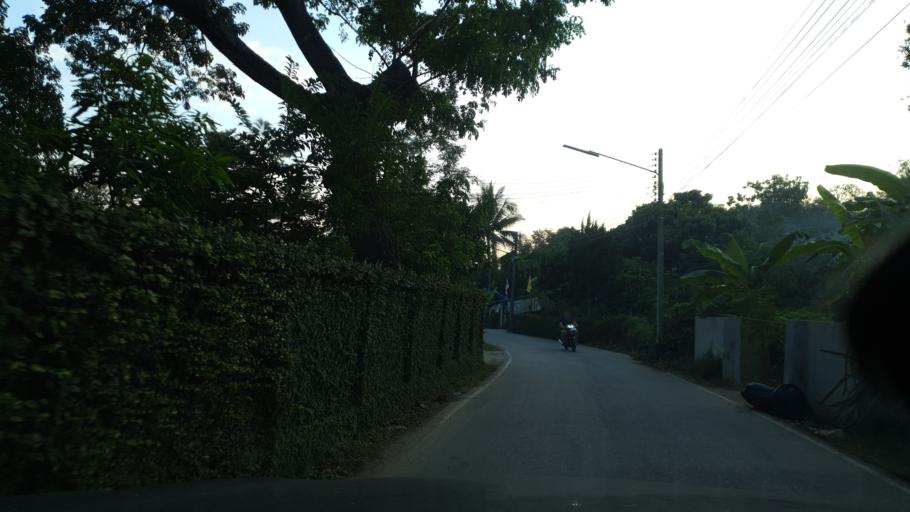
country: TH
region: Chiang Mai
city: San Sai
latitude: 18.8671
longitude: 99.0765
